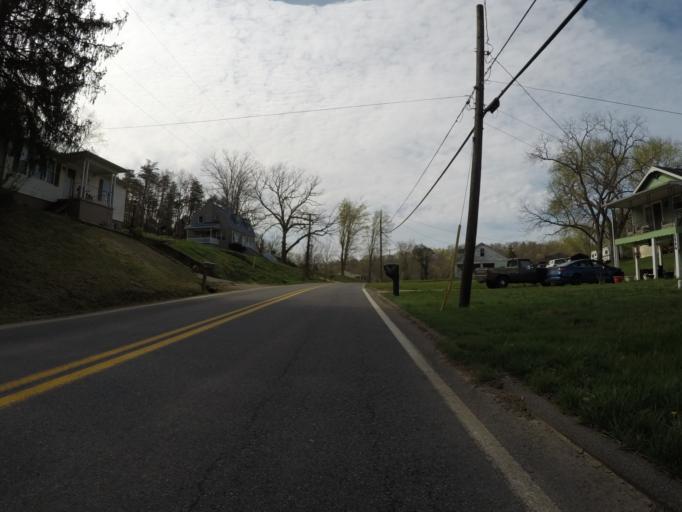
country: US
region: West Virginia
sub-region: Cabell County
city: Pea Ridge
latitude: 38.3678
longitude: -82.3726
